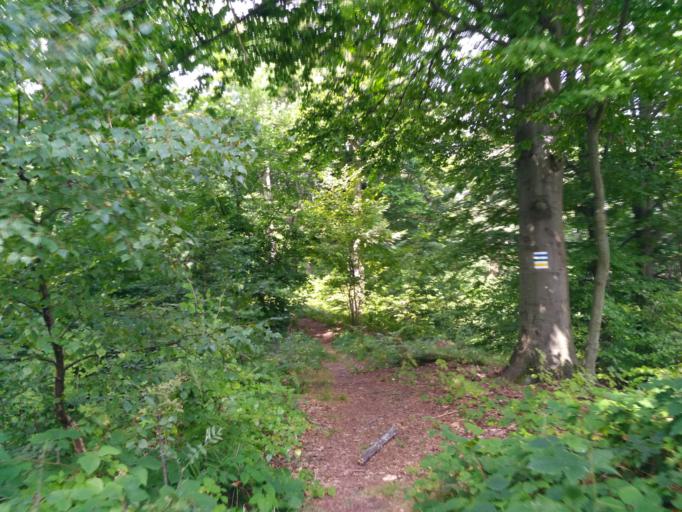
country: PL
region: Subcarpathian Voivodeship
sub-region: Powiat strzyzowski
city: Frysztak
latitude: 49.8873
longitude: 21.5413
